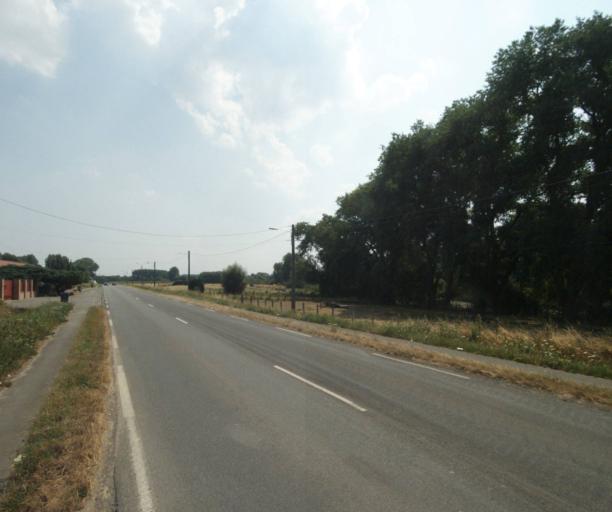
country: FR
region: Nord-Pas-de-Calais
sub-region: Departement du Nord
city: Quesnoy-sur-Deule
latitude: 50.7048
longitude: 3.0160
